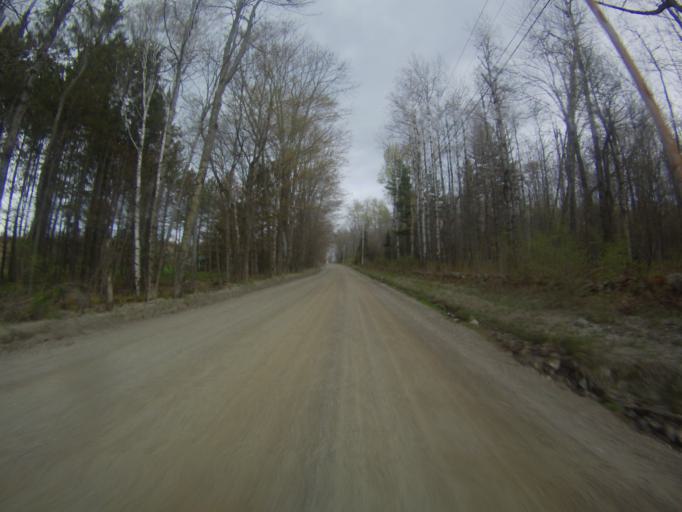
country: US
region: Vermont
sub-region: Addison County
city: Bristol
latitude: 44.0641
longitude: -73.0502
